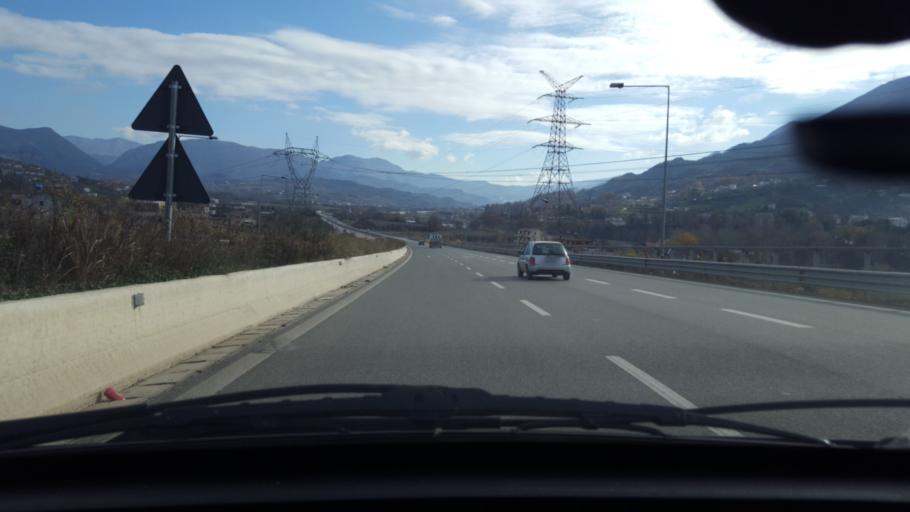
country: AL
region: Tirane
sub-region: Rrethi i Tiranes
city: Petrele
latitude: 41.2656
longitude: 19.8688
